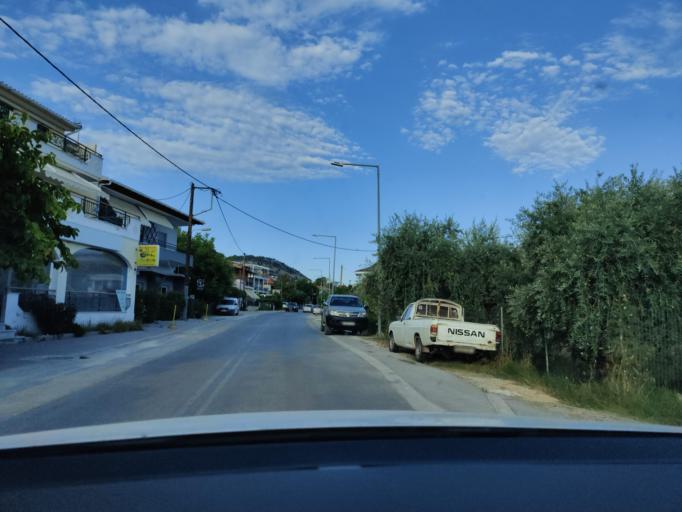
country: GR
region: East Macedonia and Thrace
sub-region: Nomos Kavalas
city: Limenaria
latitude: 40.6114
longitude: 24.6122
